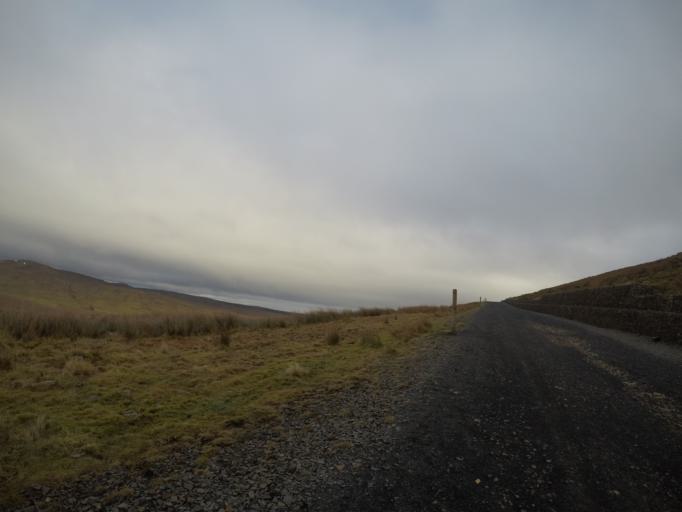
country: GB
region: Scotland
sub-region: North Ayrshire
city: Fairlie
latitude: 55.7637
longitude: -4.7958
